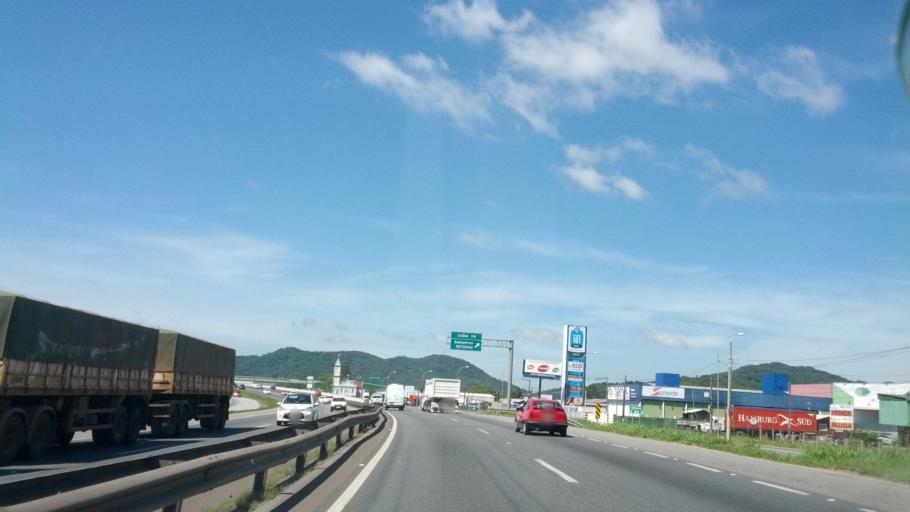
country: BR
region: Santa Catarina
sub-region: Itajai
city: Itajai
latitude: -26.8659
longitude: -48.7299
